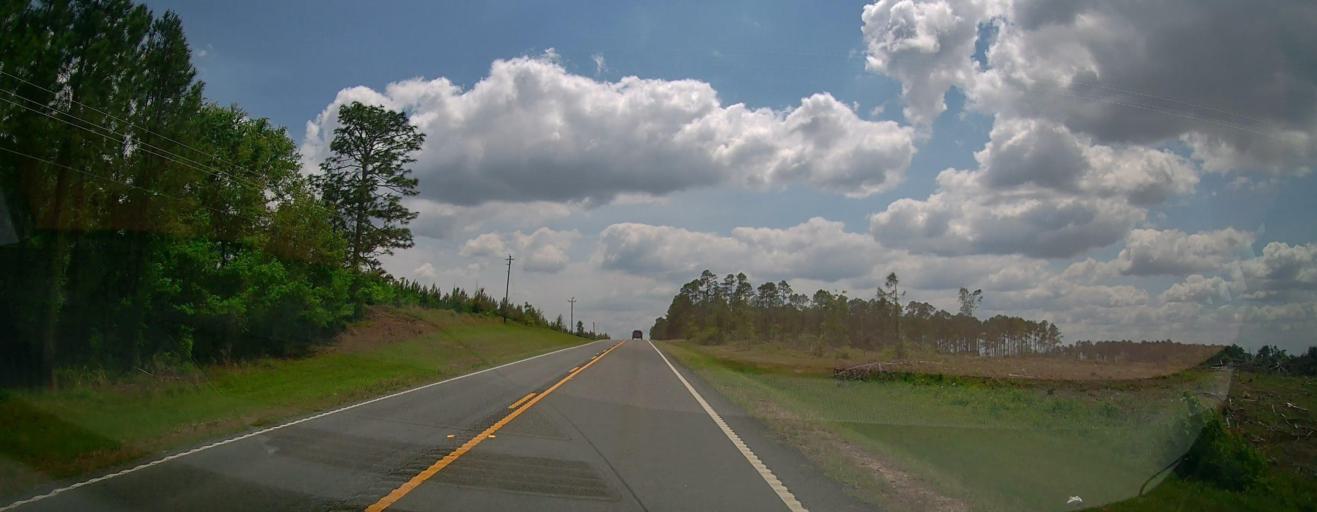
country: US
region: Georgia
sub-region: Treutlen County
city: Soperton
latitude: 32.4242
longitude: -82.6082
